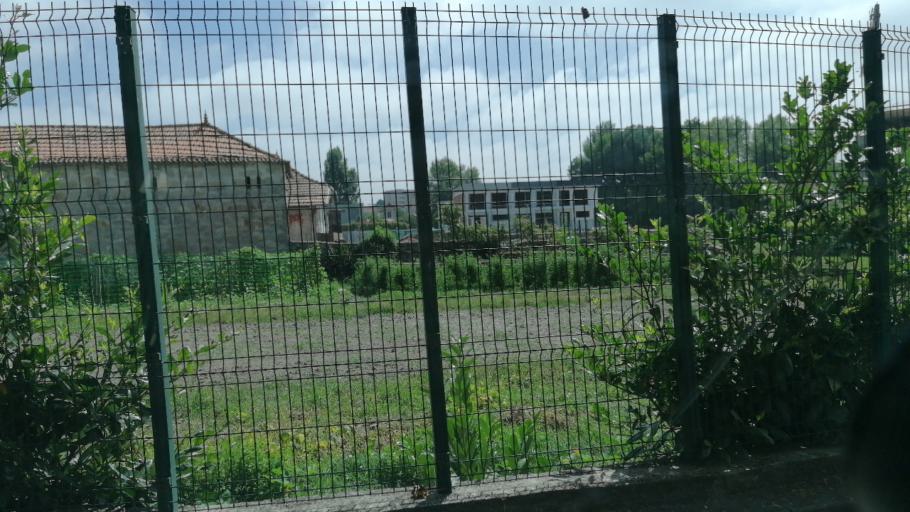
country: PT
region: Porto
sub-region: Matosinhos
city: Senhora da Hora
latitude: 41.1761
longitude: -8.6439
